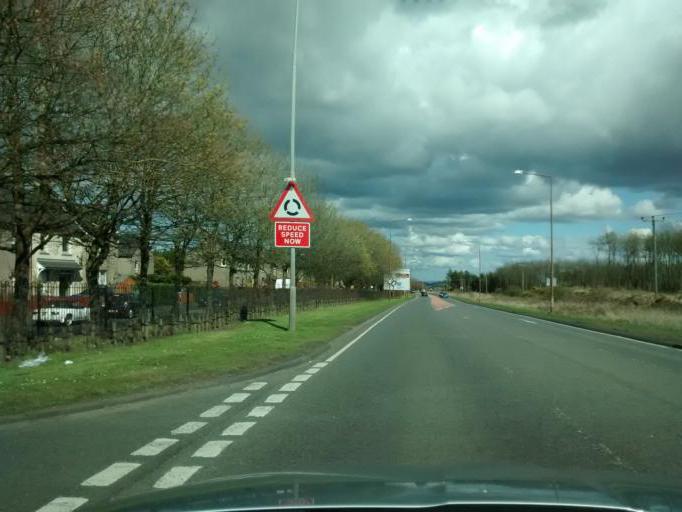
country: GB
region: Scotland
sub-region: West Lothian
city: Livingston
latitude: 55.9200
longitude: -3.5344
